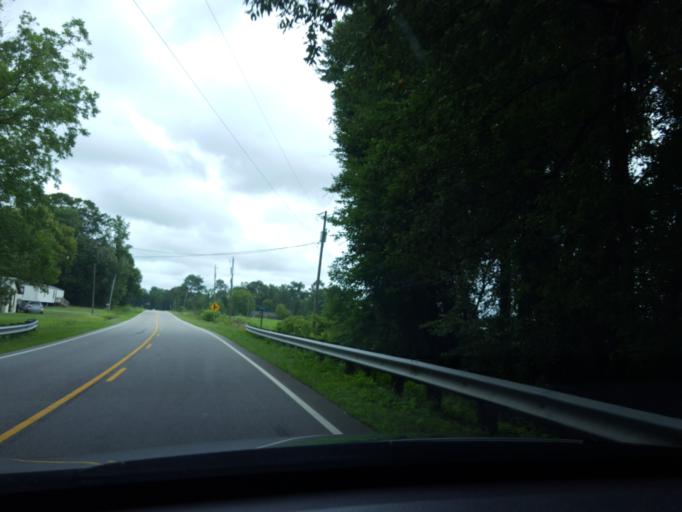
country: US
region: North Carolina
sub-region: Martin County
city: Williamston
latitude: 35.7680
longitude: -76.9527
